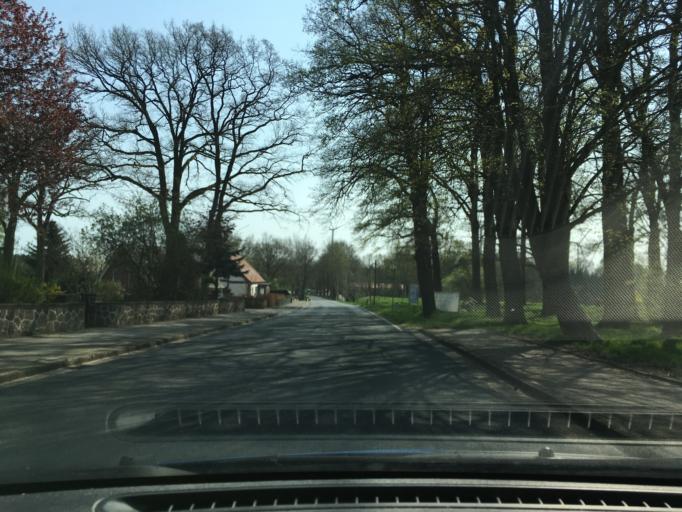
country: DE
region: Lower Saxony
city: Sudergellersen
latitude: 53.2062
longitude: 10.3003
